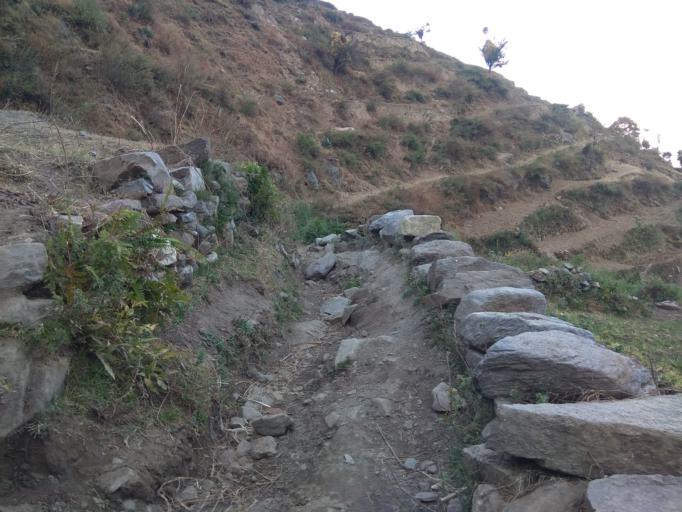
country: NP
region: Mid Western
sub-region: Karnali Zone
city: Jumla
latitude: 29.3235
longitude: 81.7205
